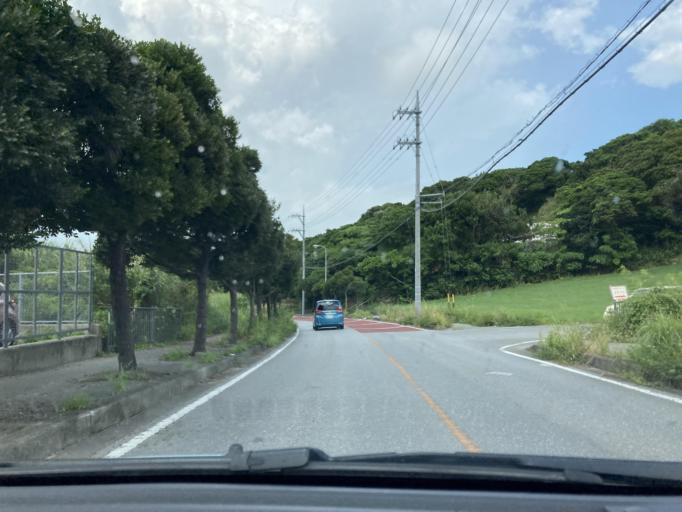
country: JP
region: Okinawa
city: Tomigusuku
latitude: 26.1721
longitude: 127.7527
